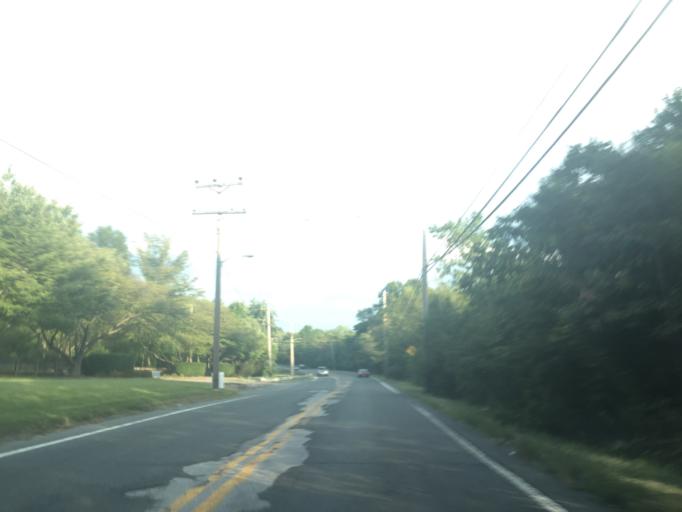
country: US
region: Maryland
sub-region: Montgomery County
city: Spencerville
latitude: 39.1137
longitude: -76.9579
